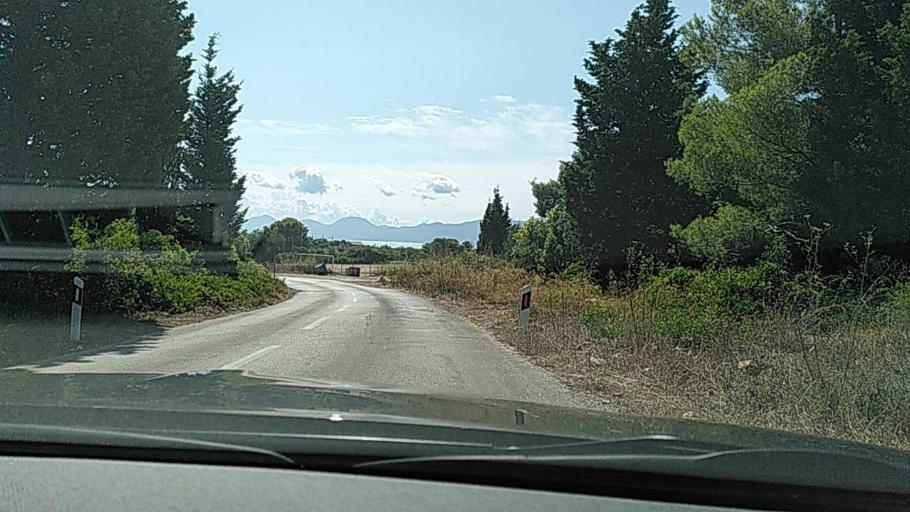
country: HR
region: Dubrovacko-Neretvanska
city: Orebic
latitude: 43.1293
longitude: 17.1758
